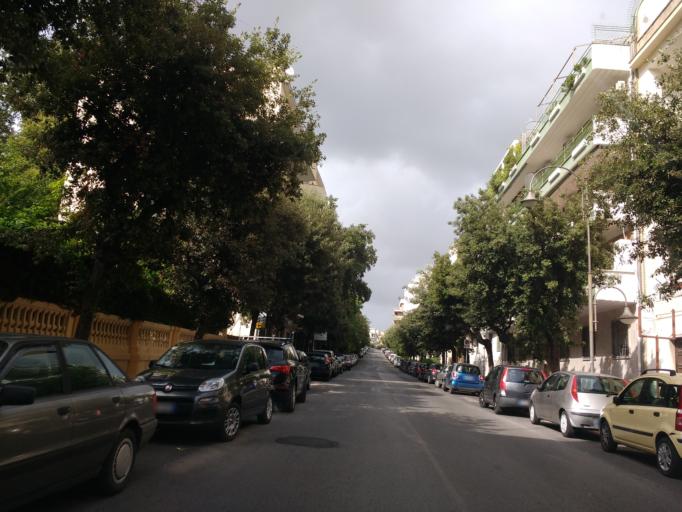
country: IT
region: Latium
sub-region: Citta metropolitana di Roma Capitale
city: Anzio
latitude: 41.4489
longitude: 12.6309
